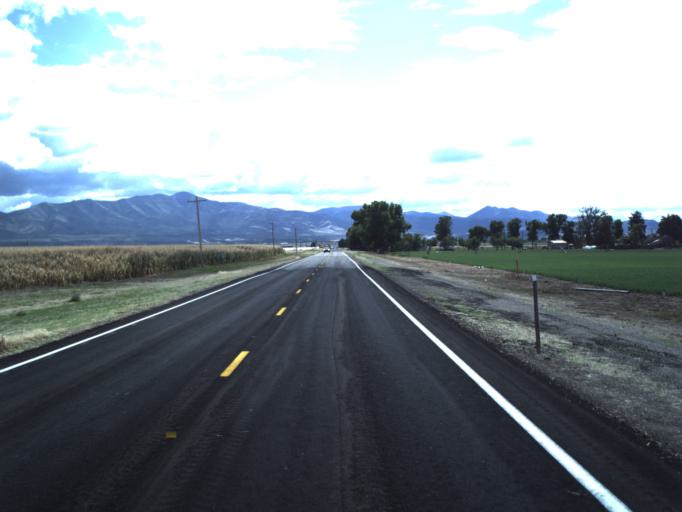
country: US
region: Utah
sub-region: Millard County
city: Fillmore
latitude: 38.8649
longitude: -112.4173
